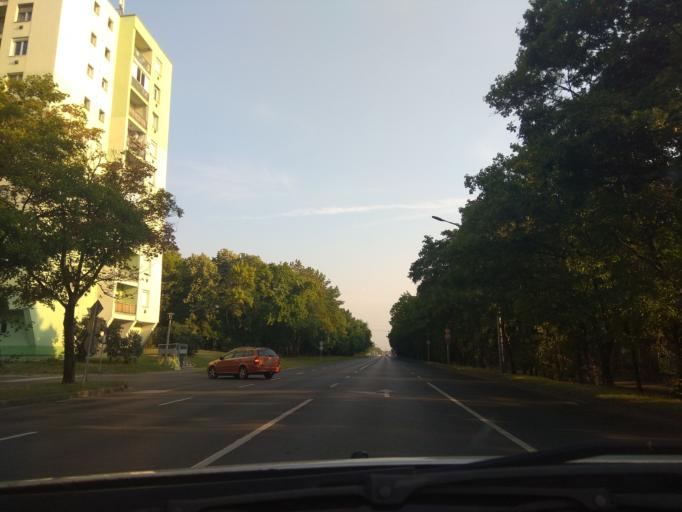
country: HU
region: Borsod-Abauj-Zemplen
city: Miskolc
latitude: 48.1212
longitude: 20.7874
